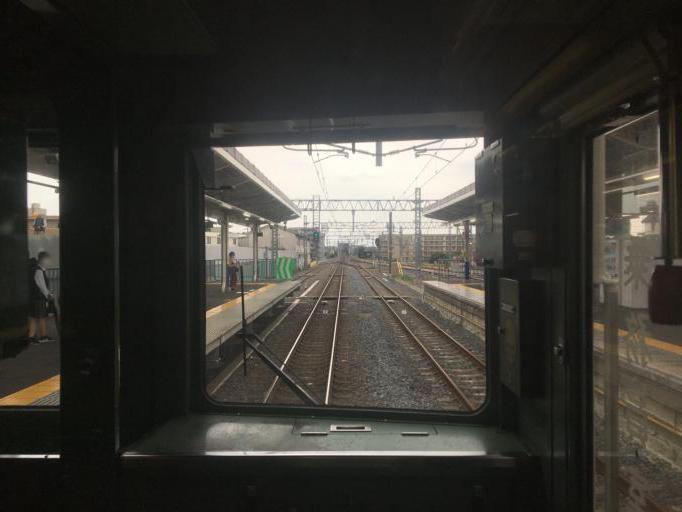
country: JP
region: Saitama
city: Iwatsuki
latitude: 35.9498
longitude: 139.6926
